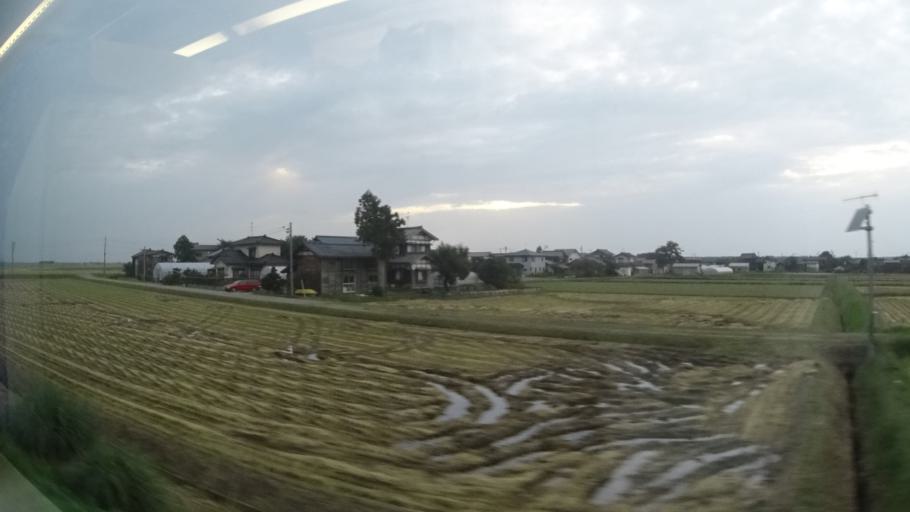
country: JP
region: Niigata
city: Murakami
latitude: 38.1739
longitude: 139.4595
